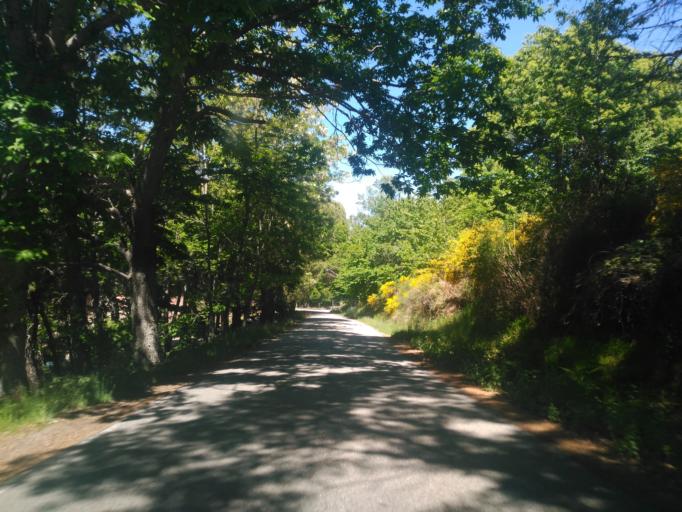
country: ES
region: Castille and Leon
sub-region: Provincia de Salamanca
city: Bejar
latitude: 40.3777
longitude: -5.7625
